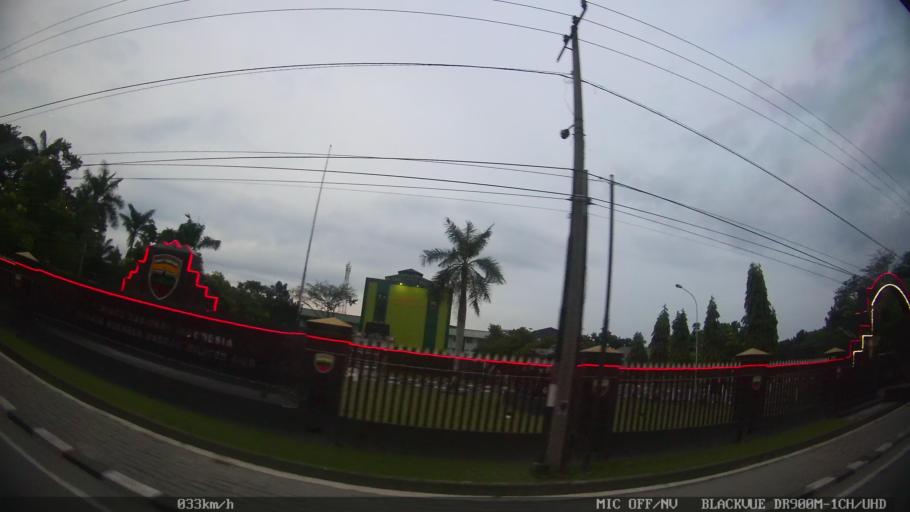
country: ID
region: North Sumatra
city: Sunggal
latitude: 3.5929
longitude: 98.6220
